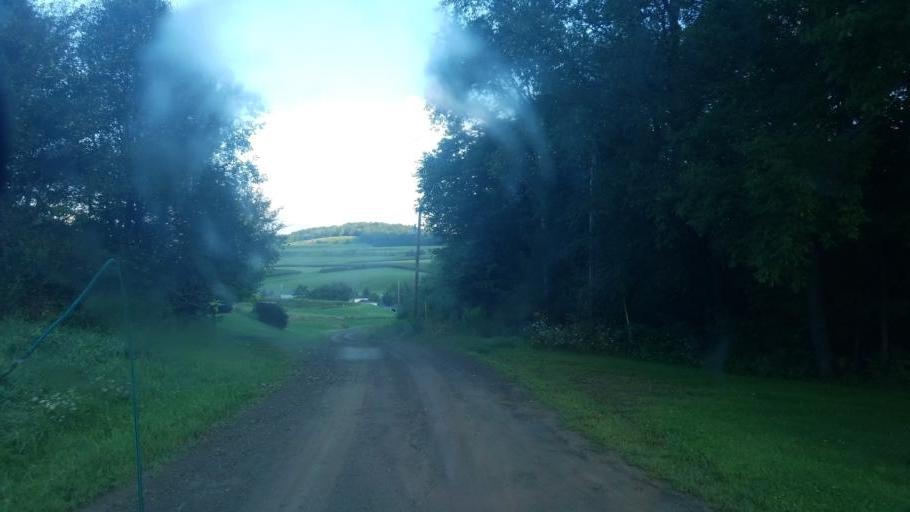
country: US
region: Pennsylvania
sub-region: Potter County
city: Galeton
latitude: 41.8789
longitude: -77.8111
